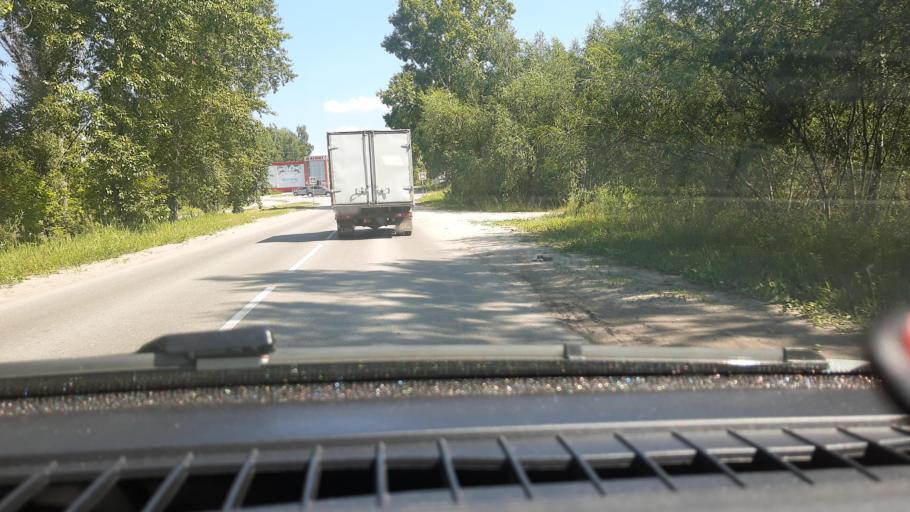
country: RU
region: Nizjnij Novgorod
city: Afonino
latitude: 56.2962
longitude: 44.1894
